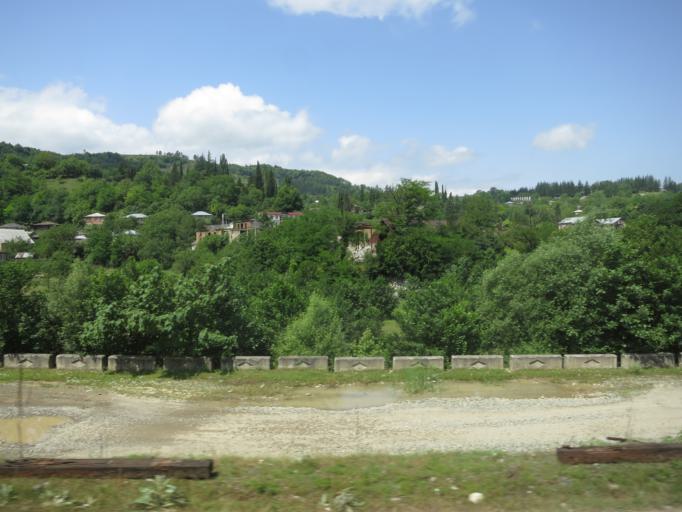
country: GE
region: Imereti
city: Kharagauli
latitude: 42.0213
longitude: 43.2036
